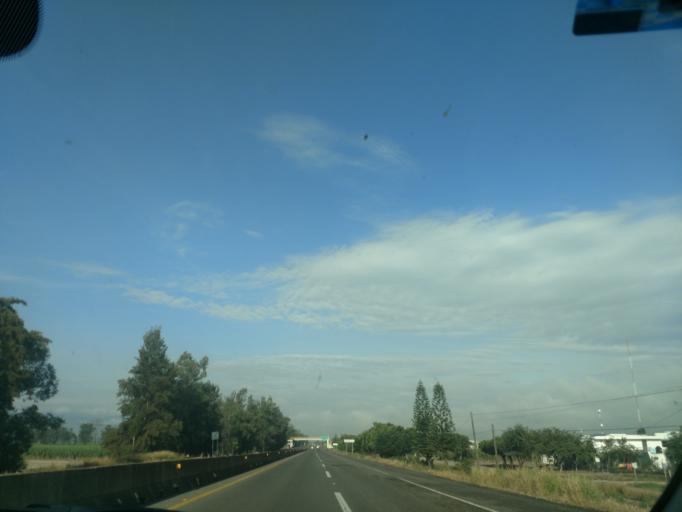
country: MX
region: Jalisco
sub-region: Ameca
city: Los Pocitos
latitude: 20.5347
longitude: -103.9624
